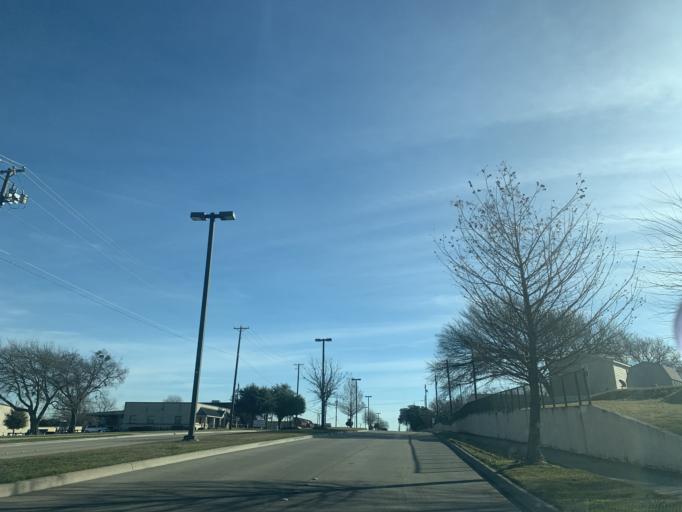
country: US
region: Texas
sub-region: Dallas County
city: DeSoto
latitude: 32.5751
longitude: -96.8286
